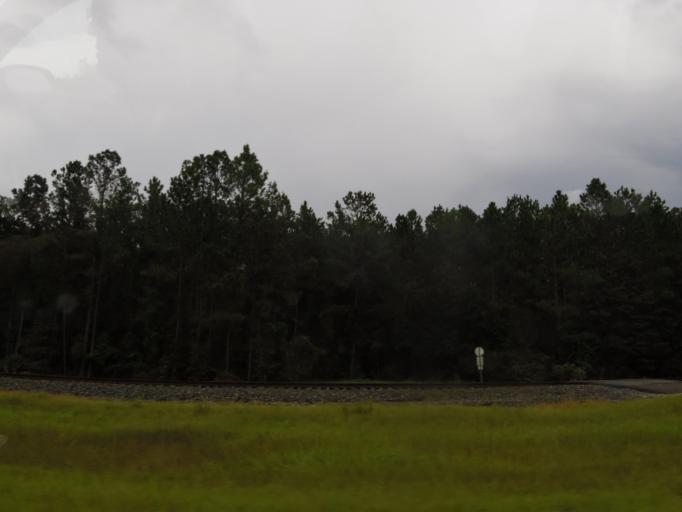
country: US
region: Georgia
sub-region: Wayne County
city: Jesup
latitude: 31.5035
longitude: -81.7585
